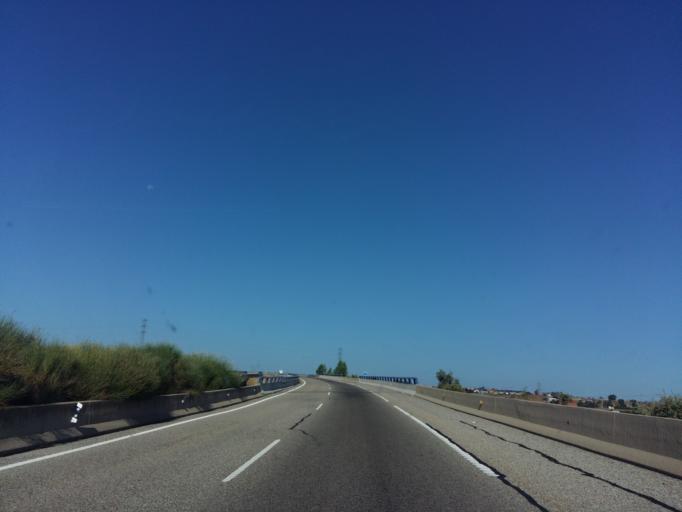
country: ES
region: Castille and Leon
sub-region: Provincia de Leon
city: San Andres del Rabanedo
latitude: 42.5764
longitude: -5.6191
